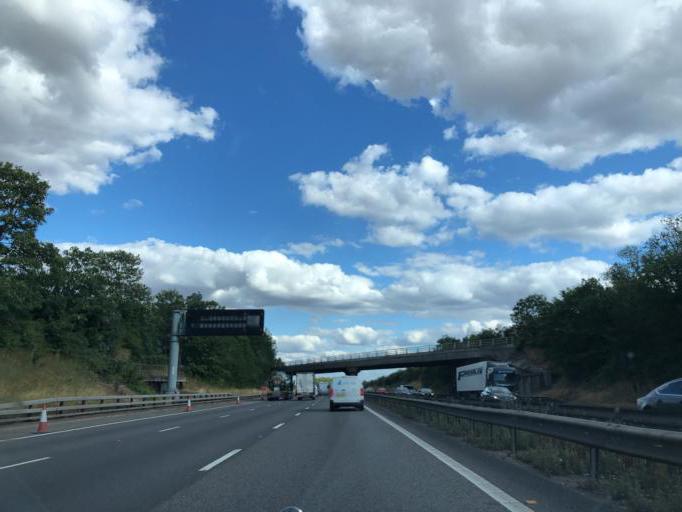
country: GB
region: England
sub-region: Milton Keynes
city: Stoke Goldington
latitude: 52.1163
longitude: -0.8000
